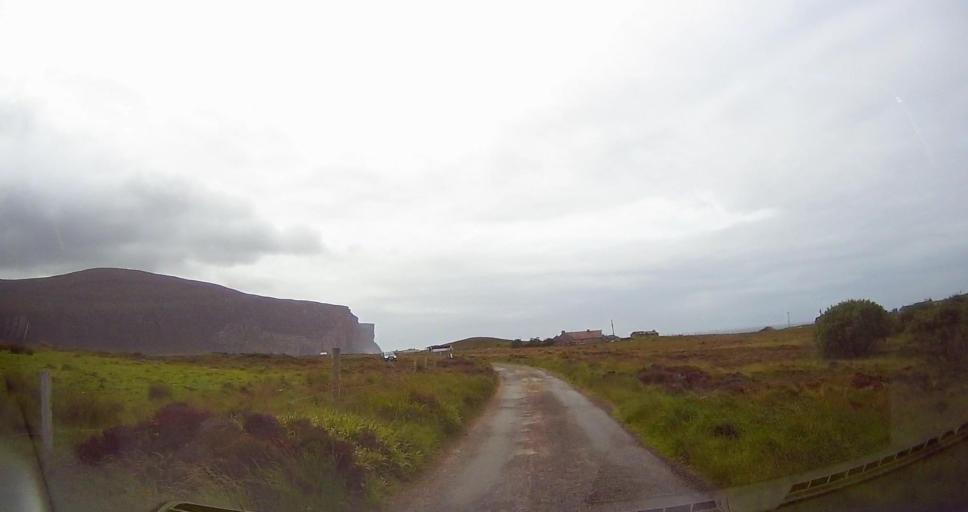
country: GB
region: Scotland
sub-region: Orkney Islands
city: Stromness
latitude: 58.8756
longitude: -3.3866
